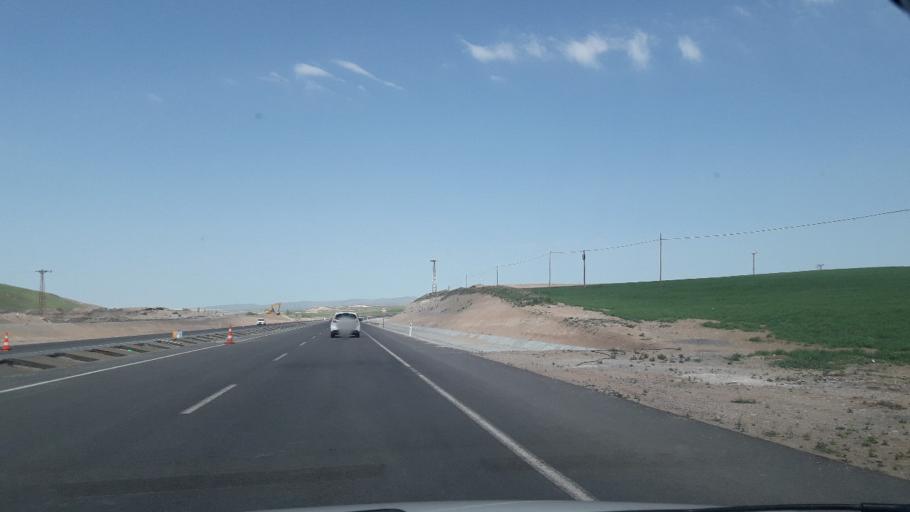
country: TR
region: Sivas
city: Deliktas
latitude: 39.2065
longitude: 37.2103
